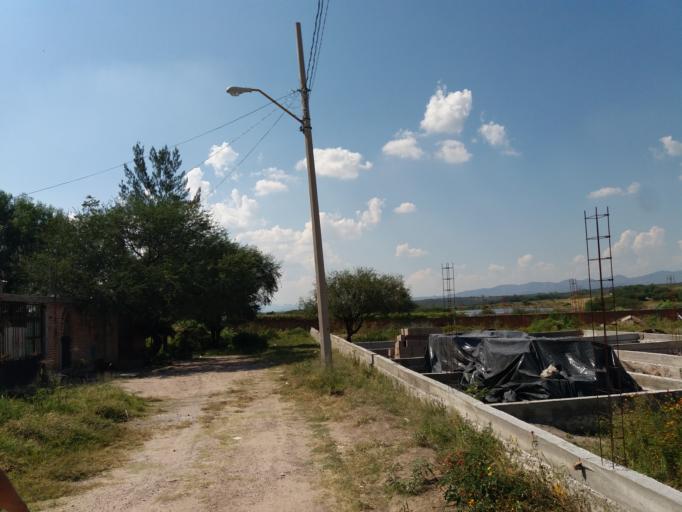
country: MX
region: Aguascalientes
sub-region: Aguascalientes
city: Penuelas (El Cienegal)
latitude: 21.7584
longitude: -102.3033
